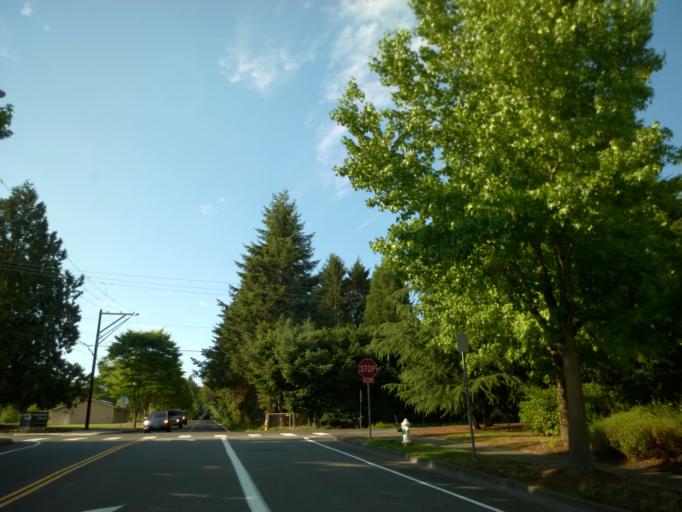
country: US
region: Washington
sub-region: King County
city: Bothell
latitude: 47.7799
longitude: -122.1858
